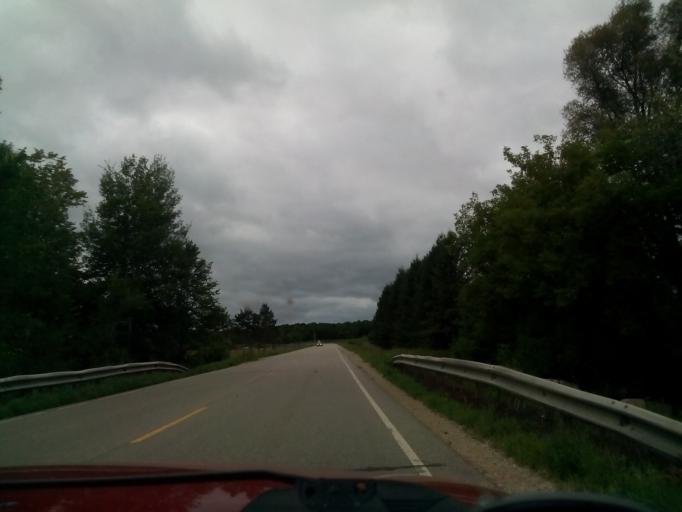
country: US
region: Wisconsin
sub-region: Menominee County
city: Legend Lake
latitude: 44.9984
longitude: -88.4308
